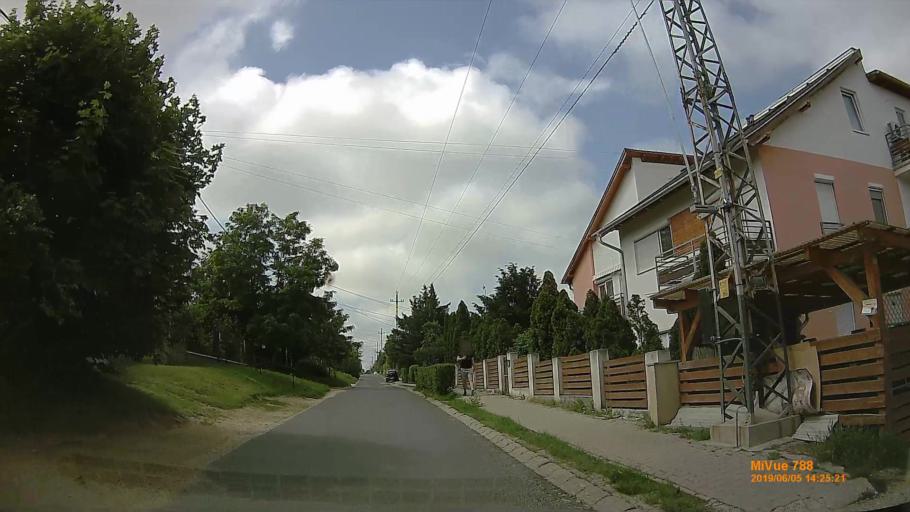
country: HU
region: Pest
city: Kistarcsa
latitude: 47.5543
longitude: 19.2711
